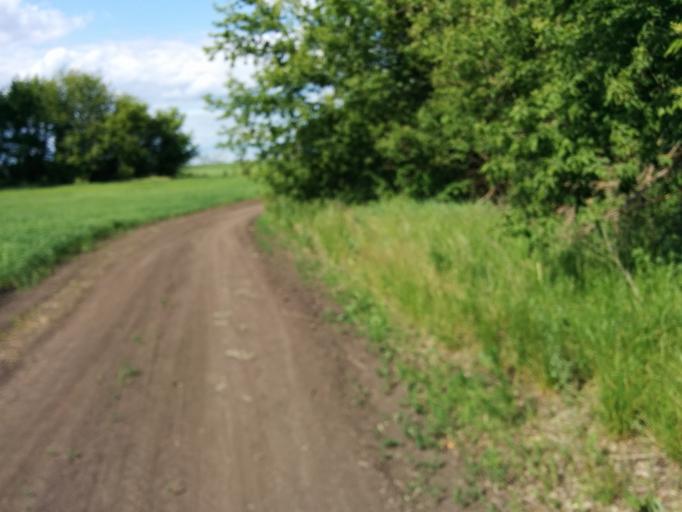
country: RU
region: Tambov
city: Tambov
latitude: 52.8053
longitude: 41.3914
